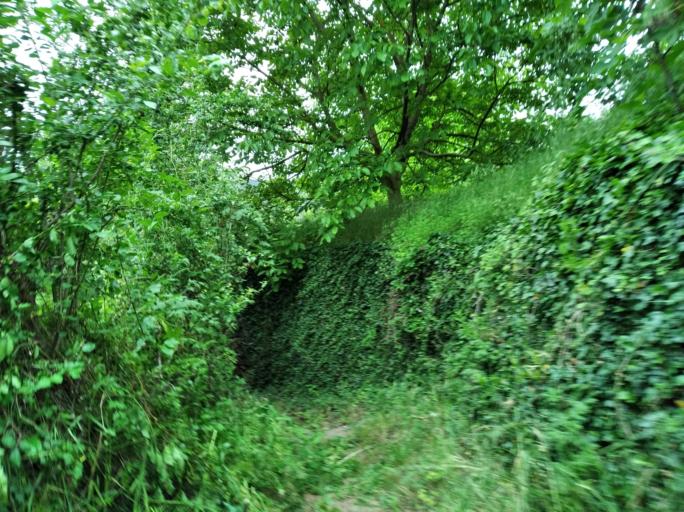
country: ES
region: La Rioja
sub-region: Provincia de La Rioja
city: Robres del Castillo
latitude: 42.2730
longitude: -2.2891
